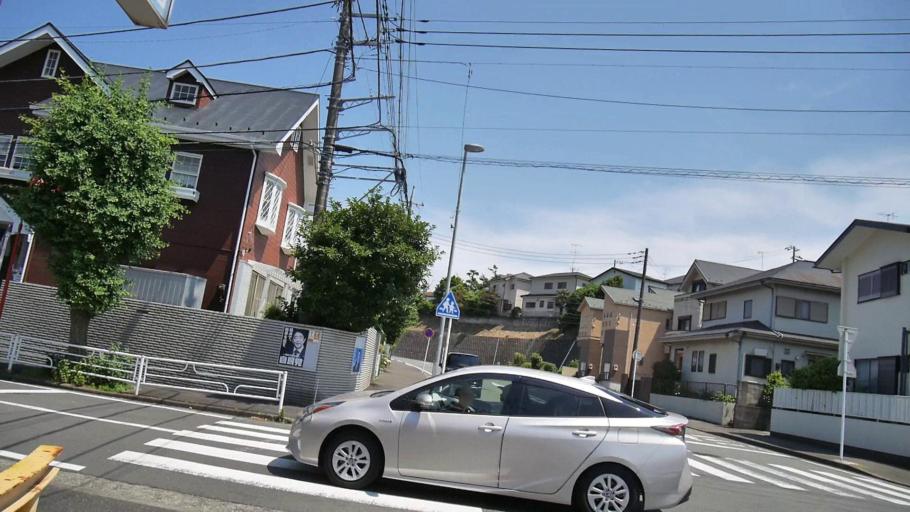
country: JP
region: Kanagawa
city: Fujisawa
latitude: 35.3972
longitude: 139.5181
